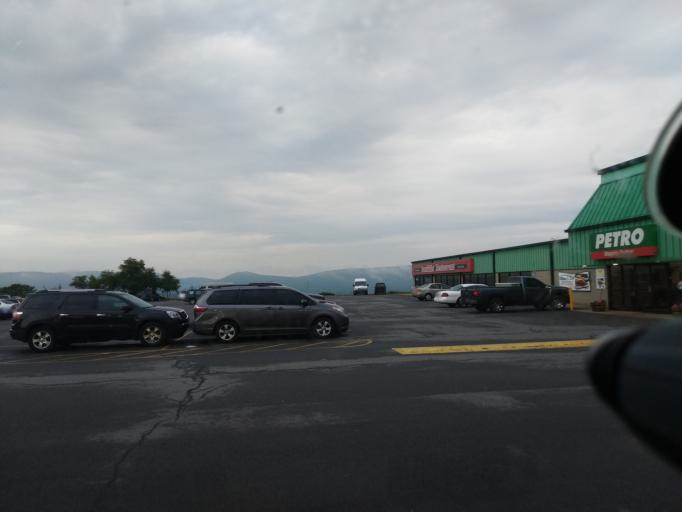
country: US
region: Pennsylvania
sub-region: Luzerne County
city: Dupont
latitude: 41.3297
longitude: -75.7417
